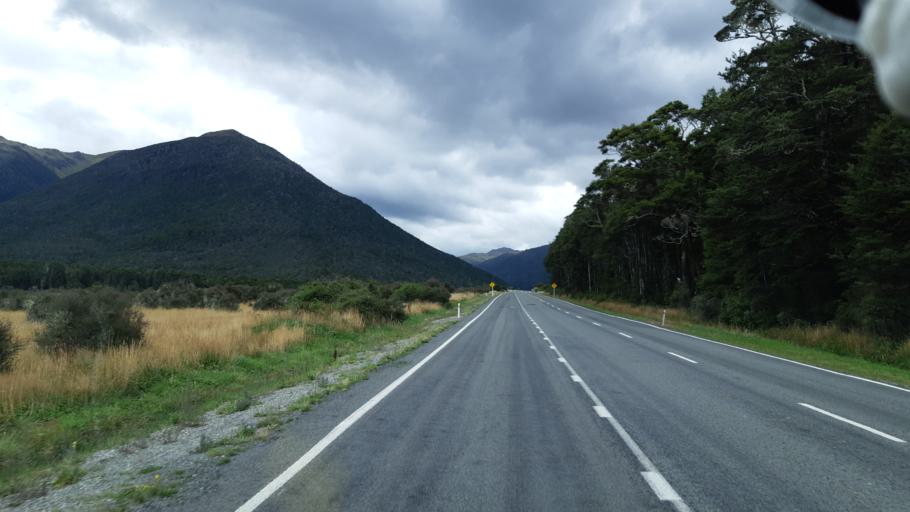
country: NZ
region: Canterbury
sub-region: Hurunui District
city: Amberley
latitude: -42.4821
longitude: 172.3908
